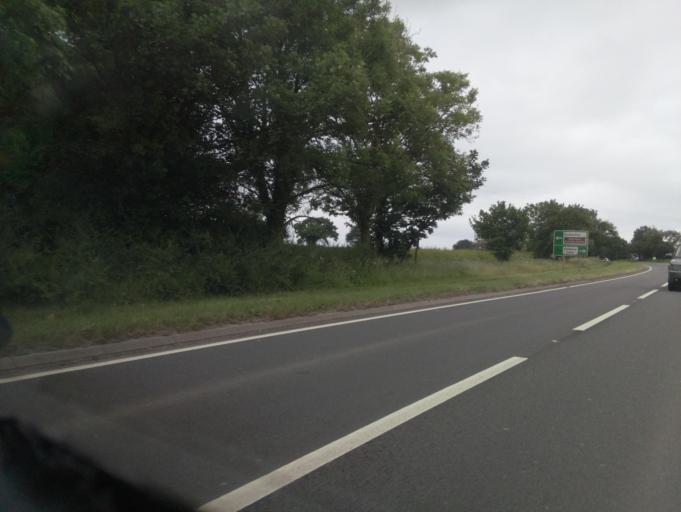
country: GB
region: England
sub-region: Derbyshire
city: Yeldersley
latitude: 52.9627
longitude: -1.6021
